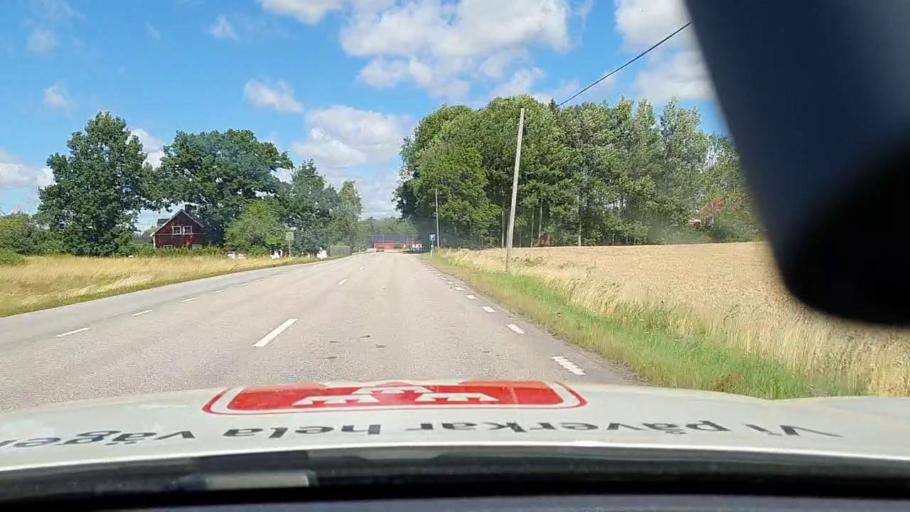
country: SE
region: Vaestra Goetaland
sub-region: Skovde Kommun
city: Stopen
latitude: 58.5135
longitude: 13.9743
